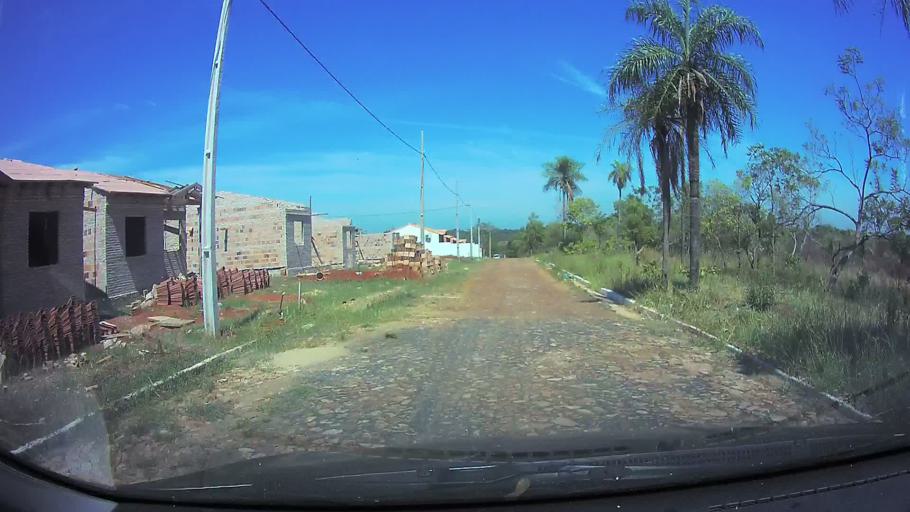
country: PY
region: Central
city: Limpio
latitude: -25.2285
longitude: -57.4362
